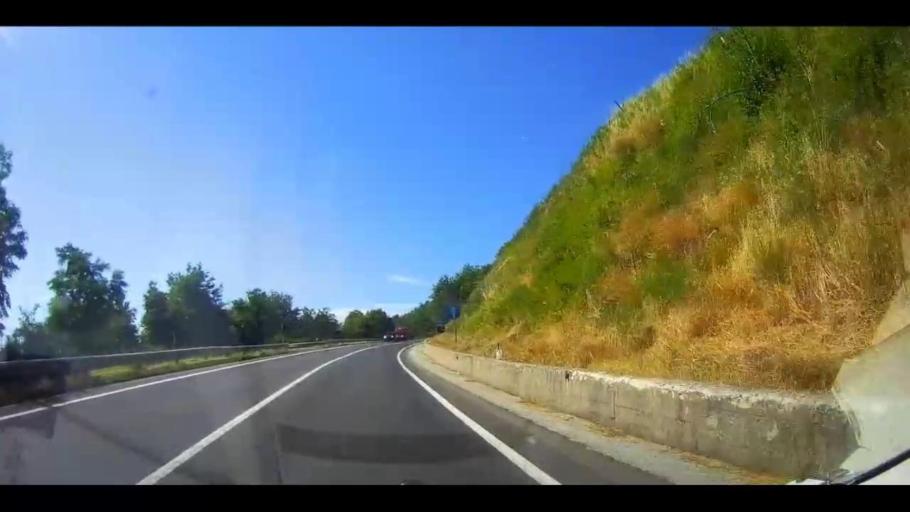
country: IT
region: Calabria
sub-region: Provincia di Cosenza
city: Celico
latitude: 39.3229
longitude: 16.3643
